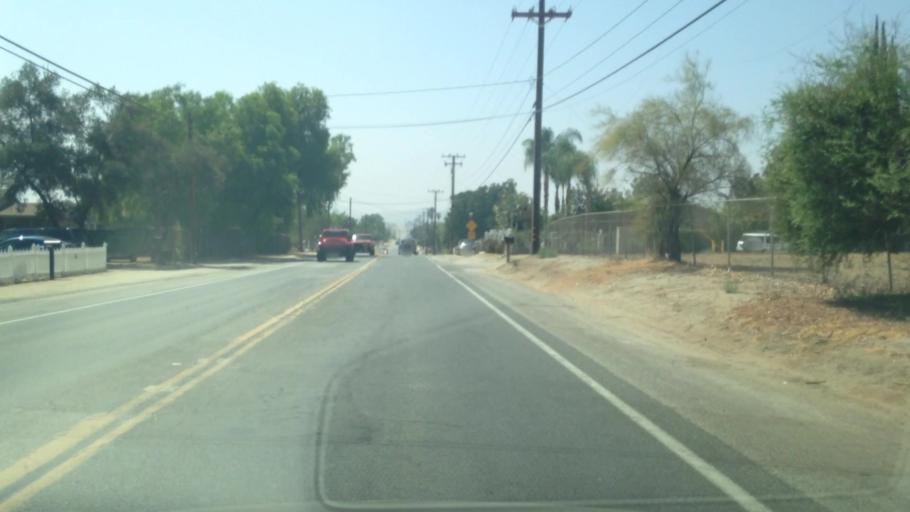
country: US
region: California
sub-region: Riverside County
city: Woodcrest
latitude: 33.8721
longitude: -117.3314
